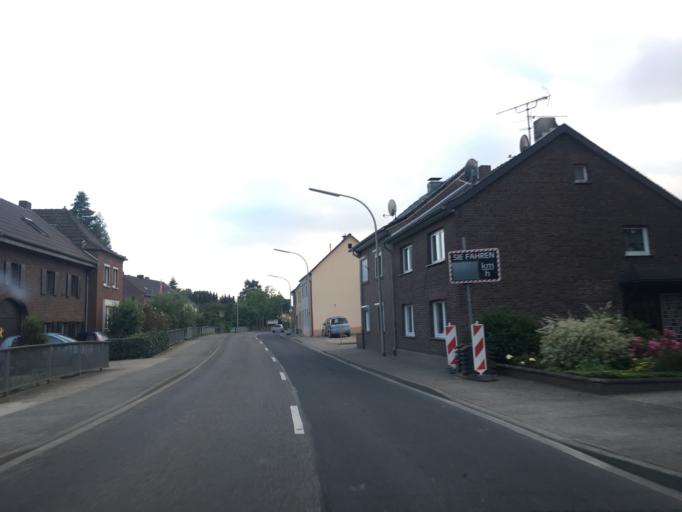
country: DE
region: North Rhine-Westphalia
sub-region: Regierungsbezirk Koln
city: Wassenberg
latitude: 51.0731
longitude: 6.1856
